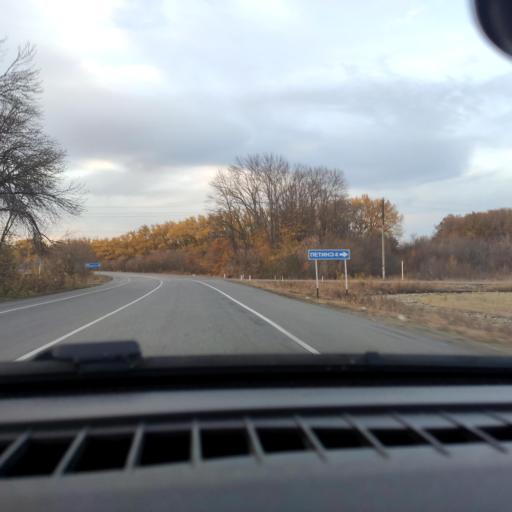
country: RU
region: Voronezj
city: Devitsa
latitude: 51.5925
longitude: 38.9778
